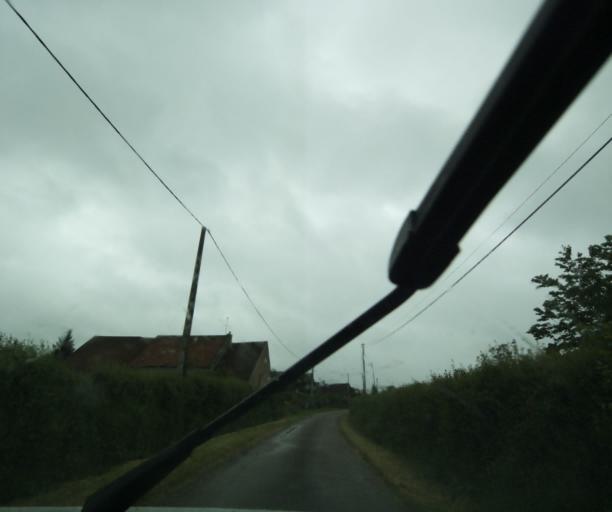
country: FR
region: Bourgogne
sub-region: Departement de Saone-et-Loire
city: Palinges
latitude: 46.5072
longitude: 4.1990
